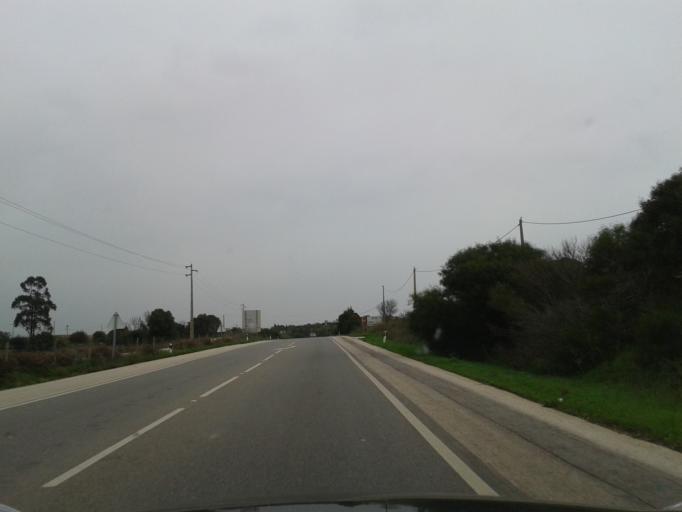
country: PT
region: Faro
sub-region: Lagos
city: Lagos
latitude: 37.1012
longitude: -8.7304
